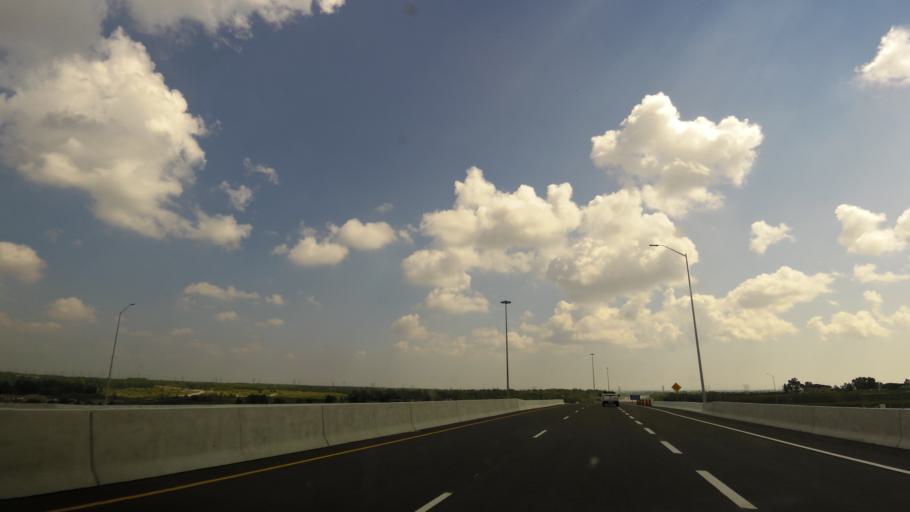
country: CA
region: Ontario
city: Ajax
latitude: 43.9428
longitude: -79.0077
